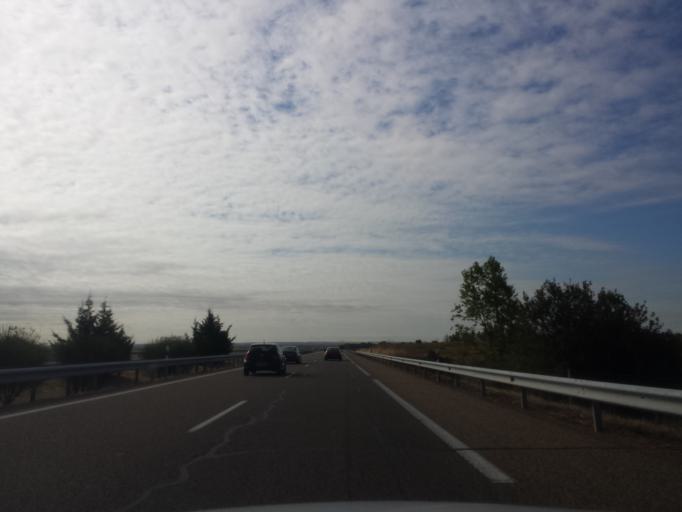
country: ES
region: Castille and Leon
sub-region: Provincia de Leon
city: Ardon
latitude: 42.4733
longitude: -5.5902
